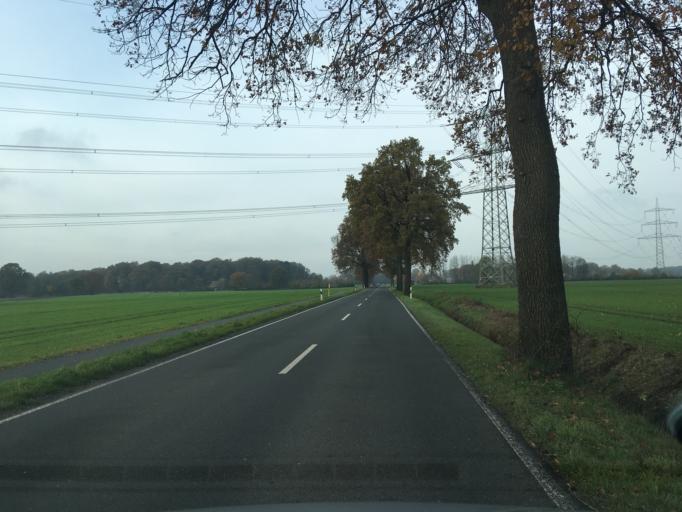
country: DE
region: North Rhine-Westphalia
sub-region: Regierungsbezirk Munster
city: Velen
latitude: 51.9038
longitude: 6.9737
